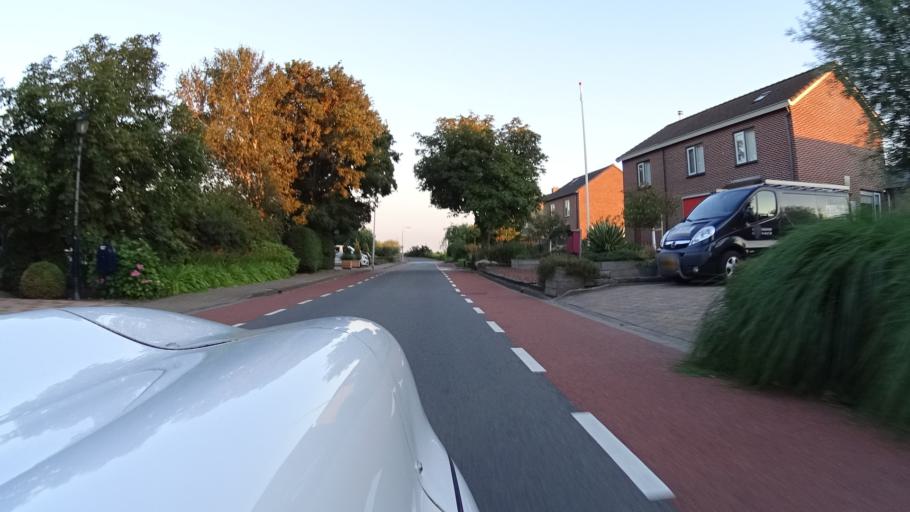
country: NL
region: South Holland
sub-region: Gemeente Kaag en Braassem
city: Oude Wetering
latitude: 52.1849
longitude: 4.6132
